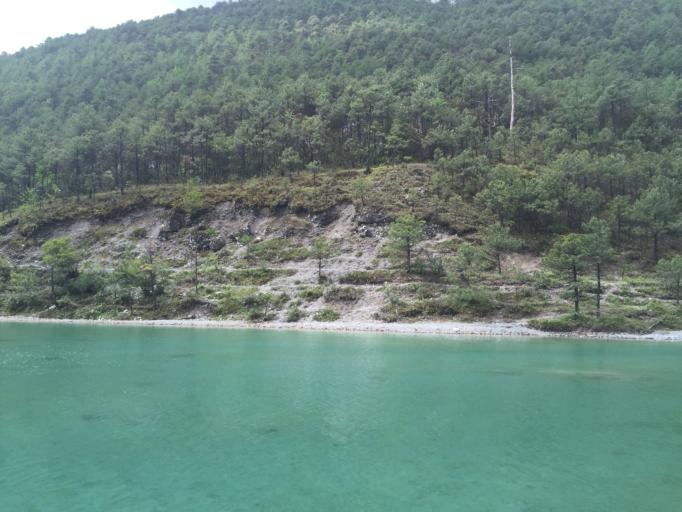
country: CN
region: Yunnan
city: Xiaqiaotou
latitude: 27.1297
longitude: 100.2394
